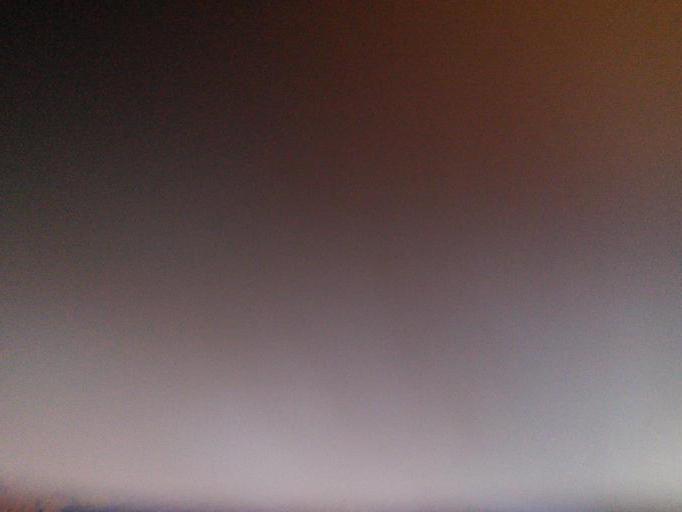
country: RU
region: Jaroslavl
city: Poshekhon'ye
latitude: 58.3764
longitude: 38.9985
